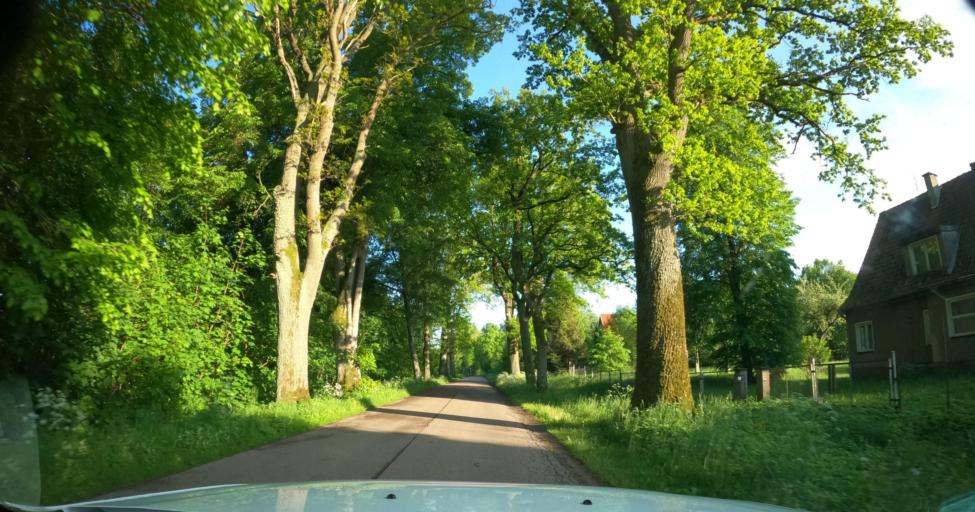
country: PL
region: Warmian-Masurian Voivodeship
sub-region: Powiat braniewski
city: Pieniezno
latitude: 54.2392
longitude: 20.0290
